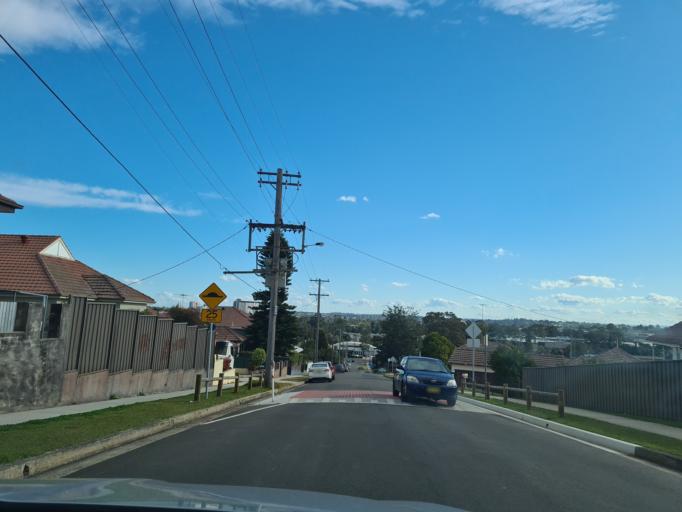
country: AU
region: New South Wales
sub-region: Parramatta
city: City of Parramatta
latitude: -33.7940
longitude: 151.0042
